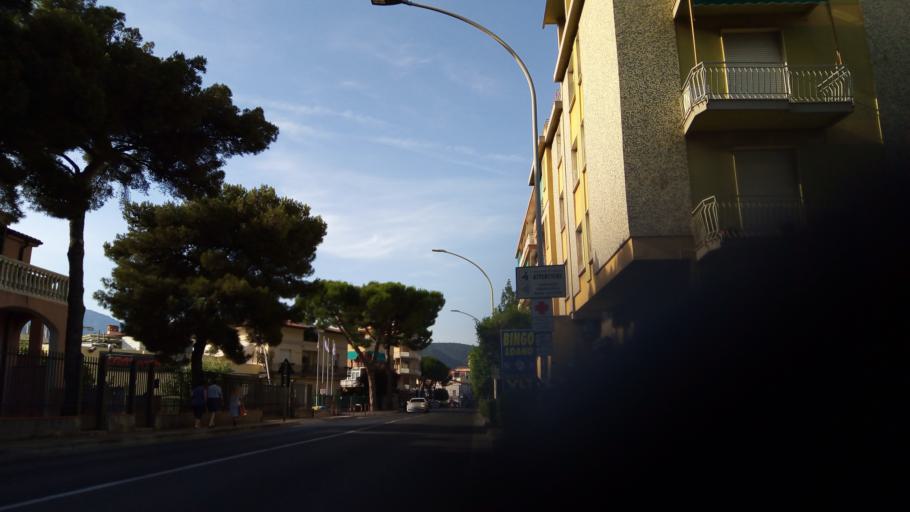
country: IT
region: Liguria
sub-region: Provincia di Savona
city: Borghetto Santo Spirito
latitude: 44.1172
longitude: 8.2485
